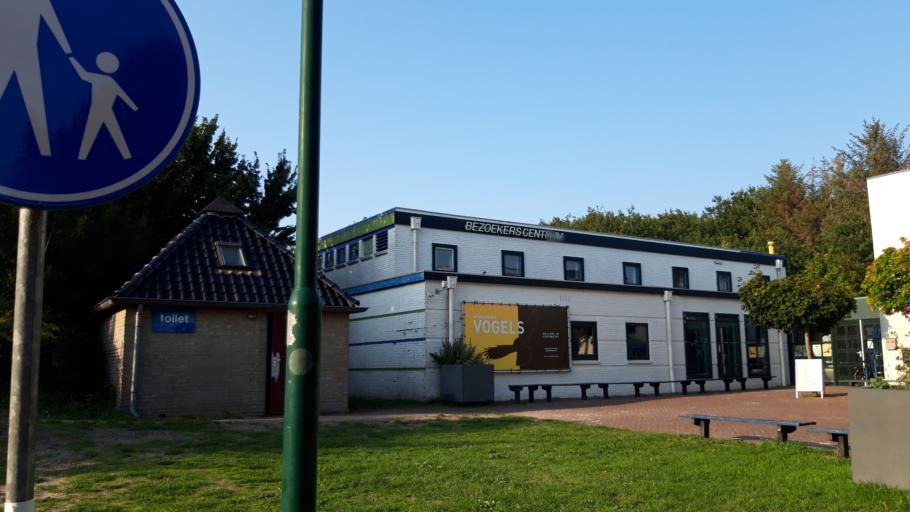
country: NL
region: Friesland
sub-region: Gemeente Schiermonnikoog
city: Schiermonnikoog
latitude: 53.4805
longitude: 6.1591
